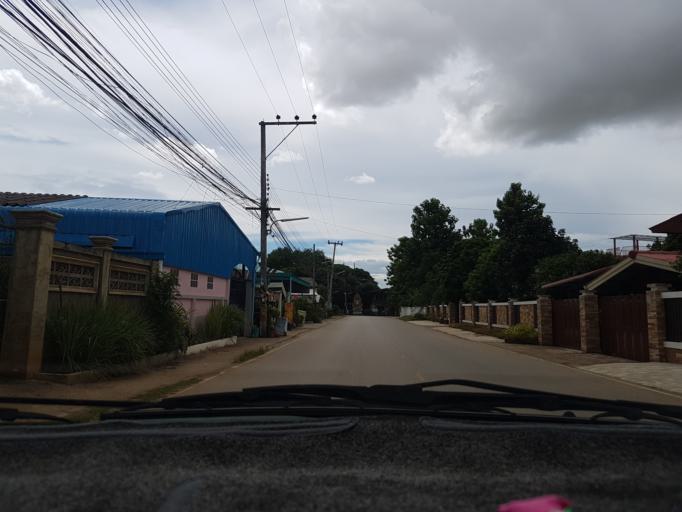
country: TH
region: Lampang
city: Ko Kha
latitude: 18.2137
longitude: 99.4140
